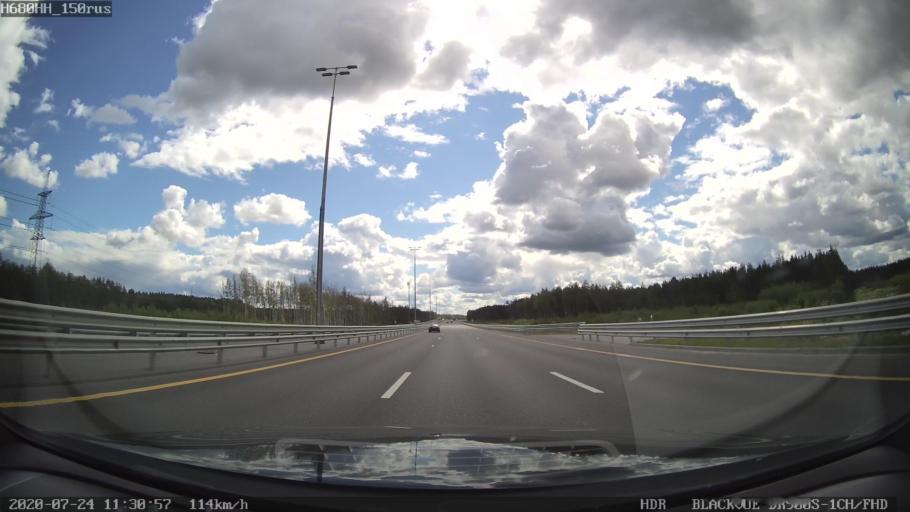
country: RU
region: Leningrad
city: Krasnyy Bor
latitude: 59.6636
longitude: 30.6233
